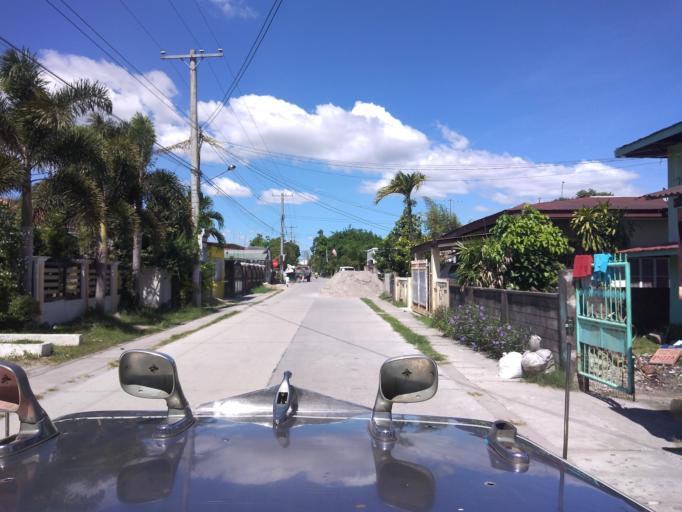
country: PH
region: Central Luzon
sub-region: Province of Pampanga
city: Magliman
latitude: 15.0398
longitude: 120.6454
